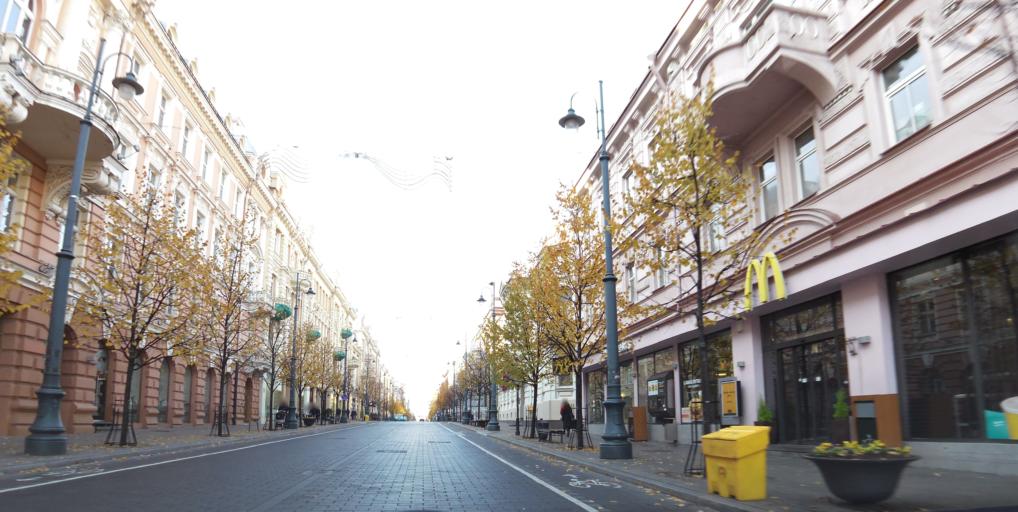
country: LT
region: Vilnius County
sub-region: Vilnius
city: Vilnius
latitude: 54.6874
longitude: 25.2786
